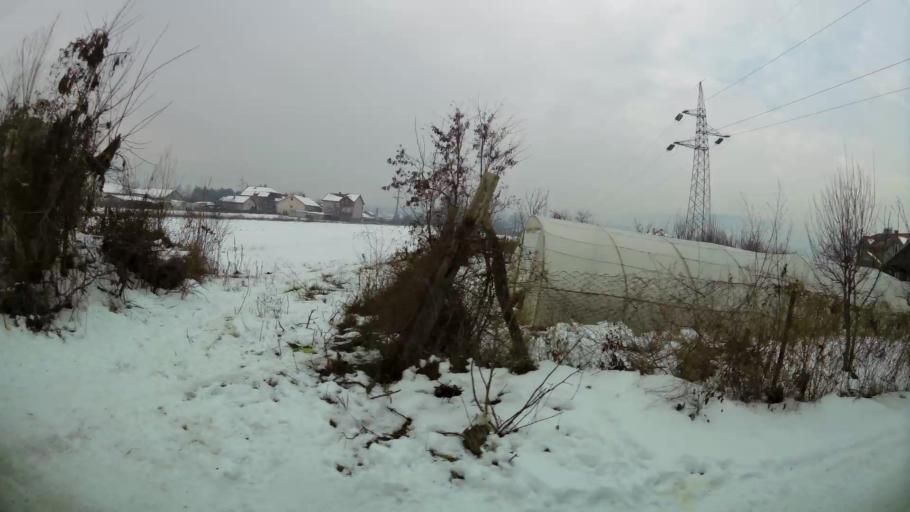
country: MK
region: Saraj
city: Saraj
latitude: 42.0426
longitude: 21.3567
